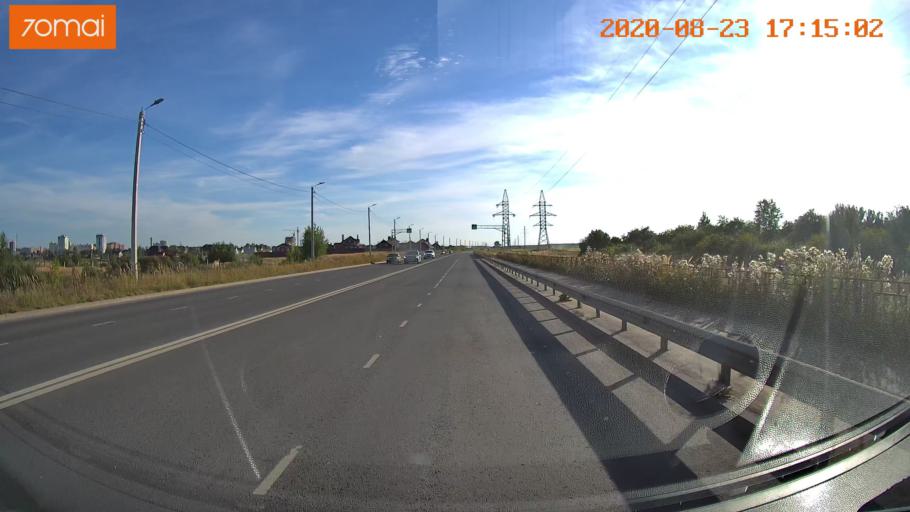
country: RU
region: Ivanovo
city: Novo-Talitsy
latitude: 57.0483
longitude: 40.9176
